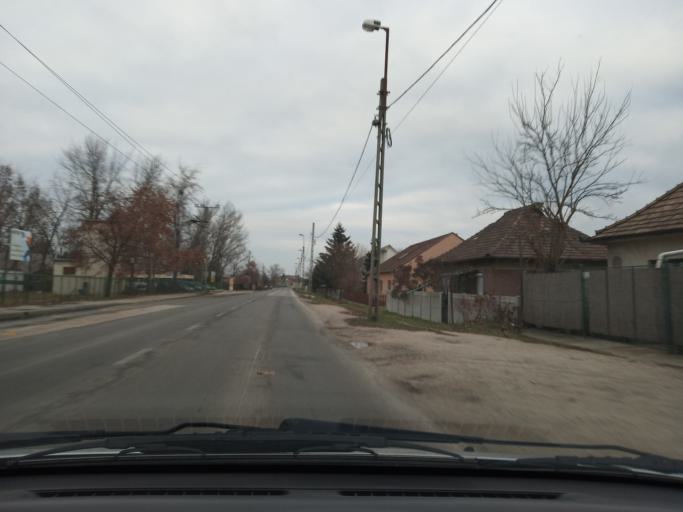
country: HU
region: Komarom-Esztergom
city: Dorog
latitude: 47.7319
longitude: 18.7252
